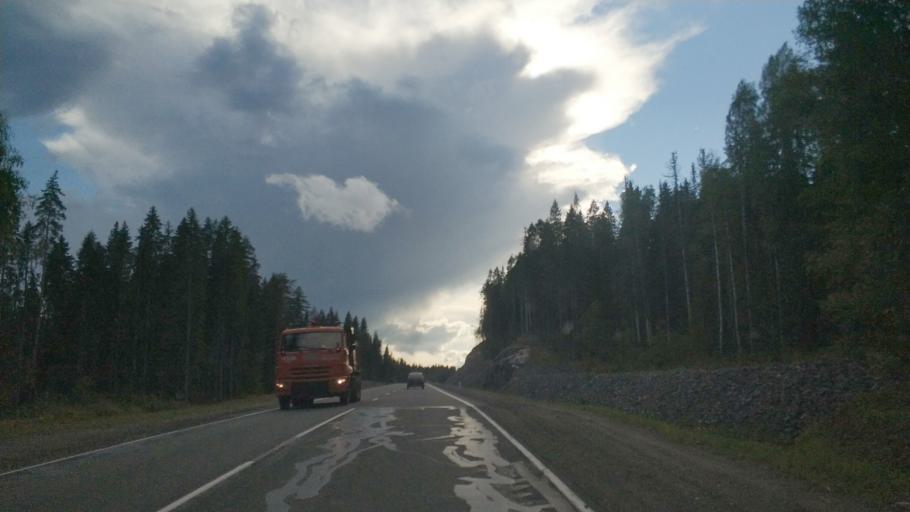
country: RU
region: Republic of Karelia
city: Lakhdenpokh'ya
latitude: 61.5099
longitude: 30.0646
